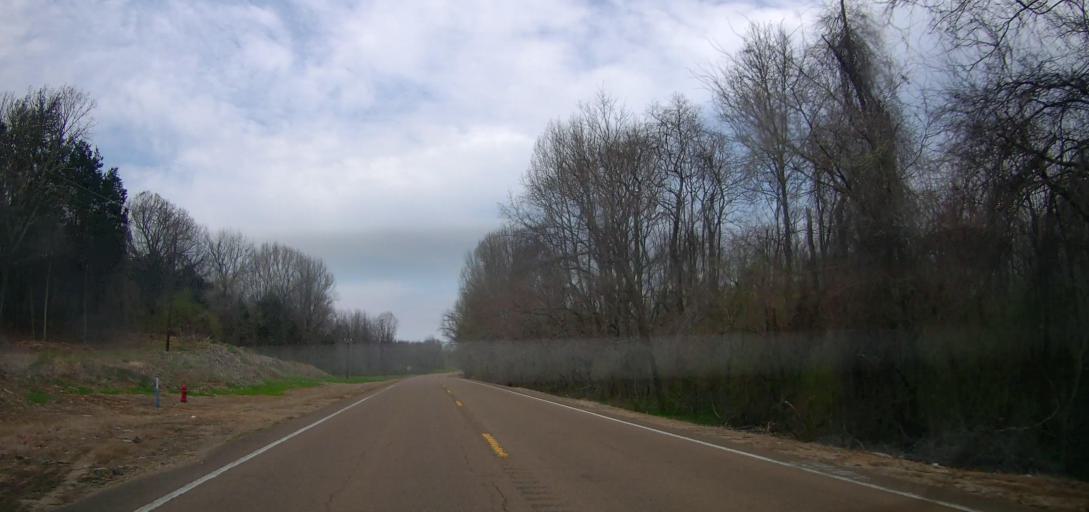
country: US
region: Mississippi
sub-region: Marshall County
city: Byhalia
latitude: 34.8478
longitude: -89.6235
